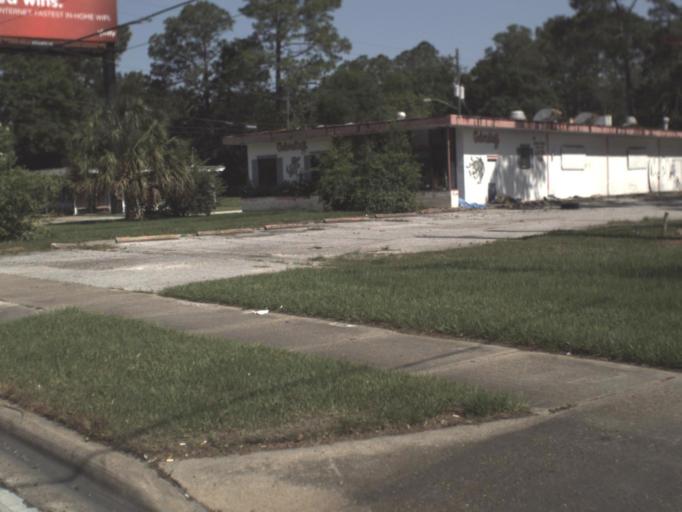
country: US
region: Florida
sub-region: Duval County
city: Jacksonville
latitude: 30.2918
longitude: -81.5991
